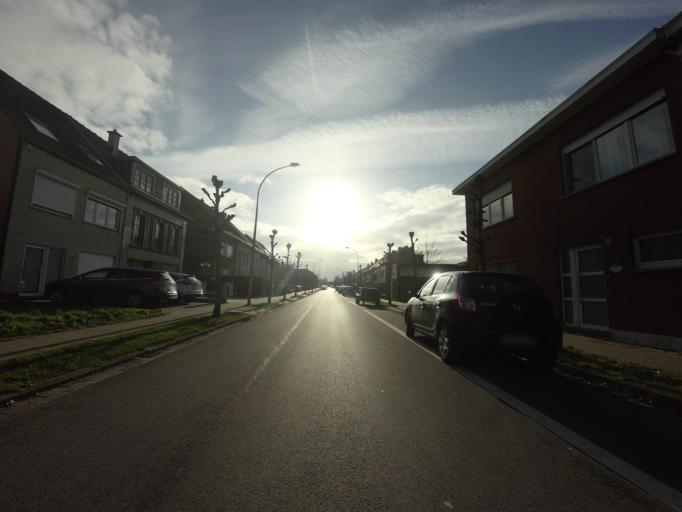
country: BE
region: Flanders
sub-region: Provincie Antwerpen
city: Schelle
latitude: 51.1287
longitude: 4.3424
